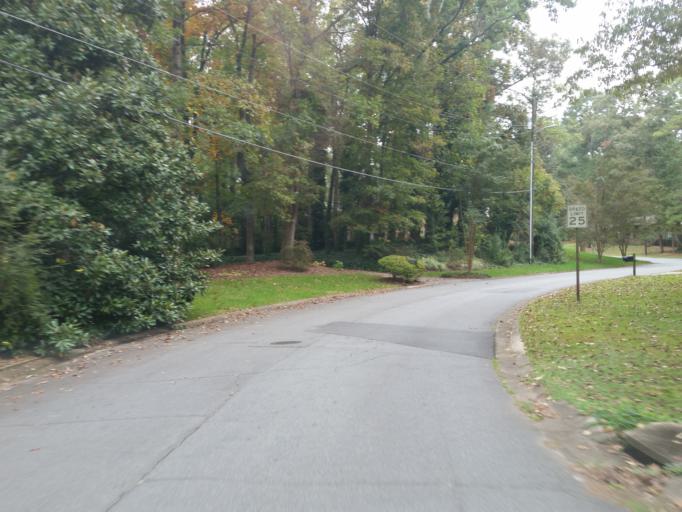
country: US
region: Georgia
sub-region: Cobb County
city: Marietta
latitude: 33.9614
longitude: -84.4740
